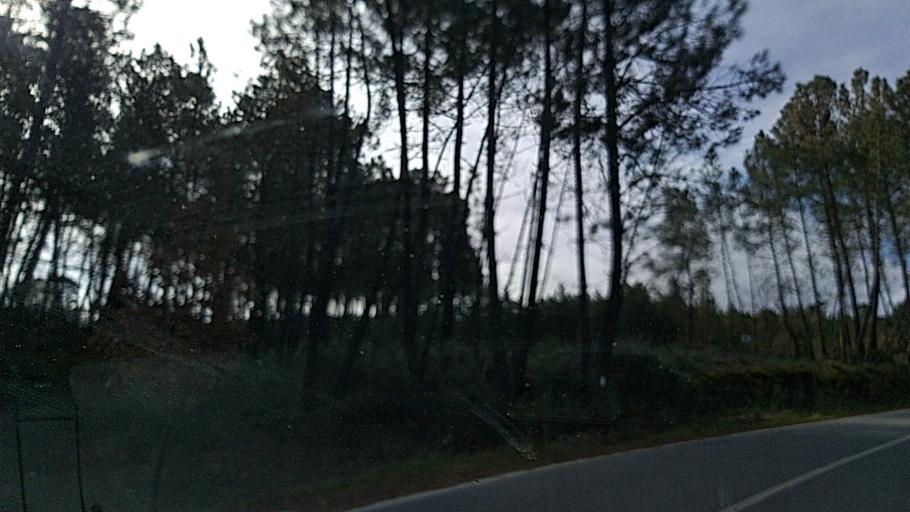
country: PT
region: Guarda
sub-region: Fornos de Algodres
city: Fornos de Algodres
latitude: 40.6965
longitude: -7.5592
